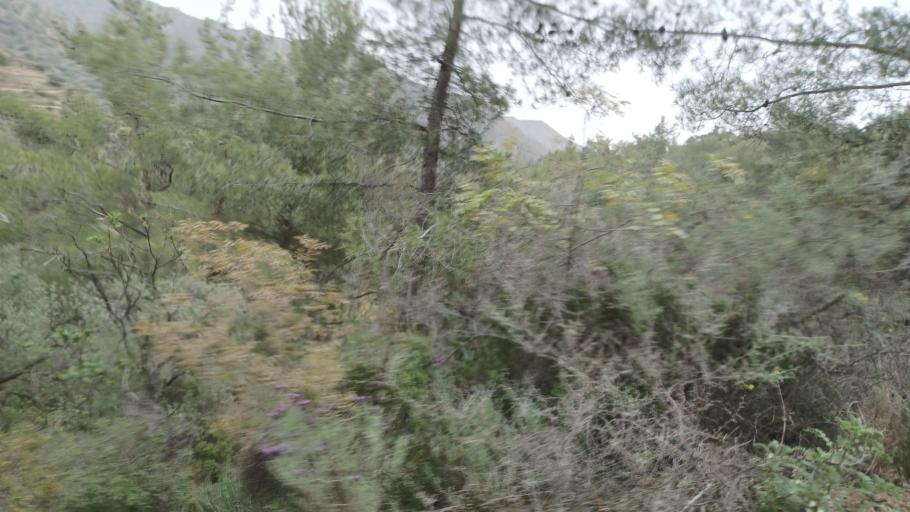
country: CY
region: Limassol
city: Parekklisha
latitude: 34.8594
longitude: 33.1065
